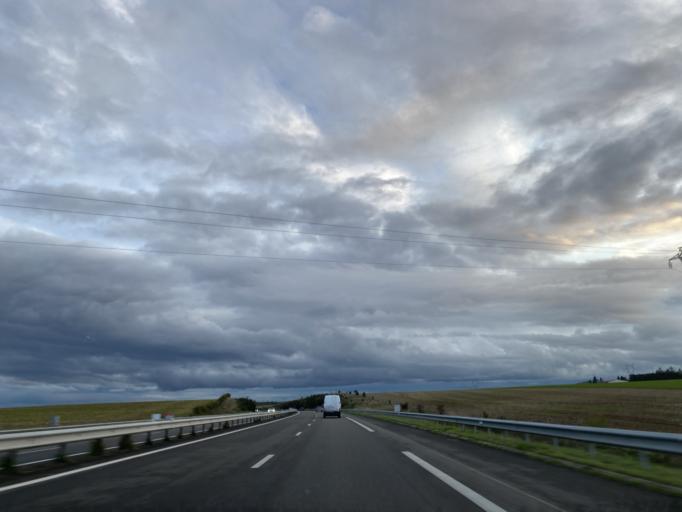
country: FR
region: Centre
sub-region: Departement du Cher
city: Trouy
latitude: 47.0177
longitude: 2.3817
